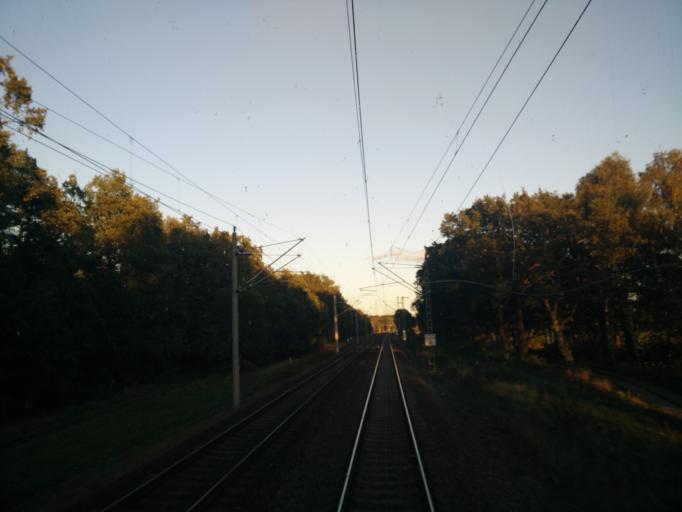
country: DE
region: Brandenburg
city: Breese
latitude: 52.9897
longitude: 11.8444
